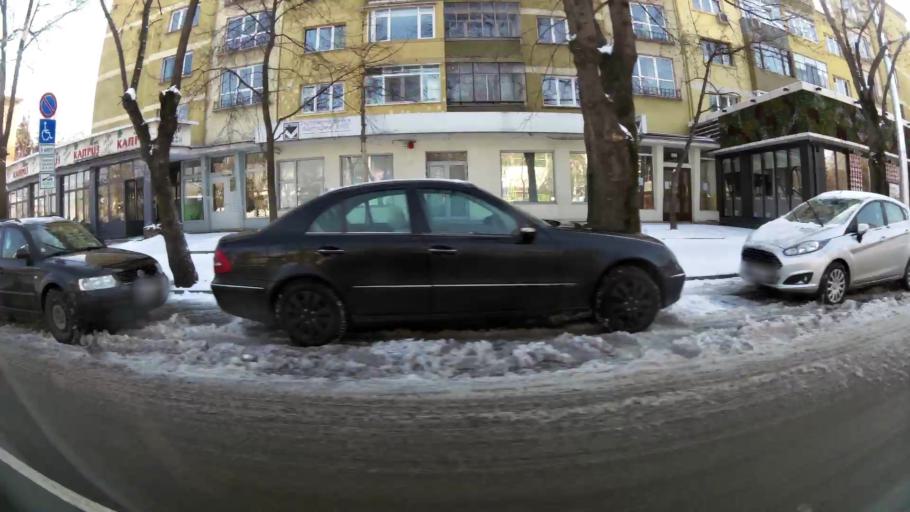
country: BG
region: Sofia-Capital
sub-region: Stolichna Obshtina
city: Sofia
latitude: 42.6744
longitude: 23.3135
